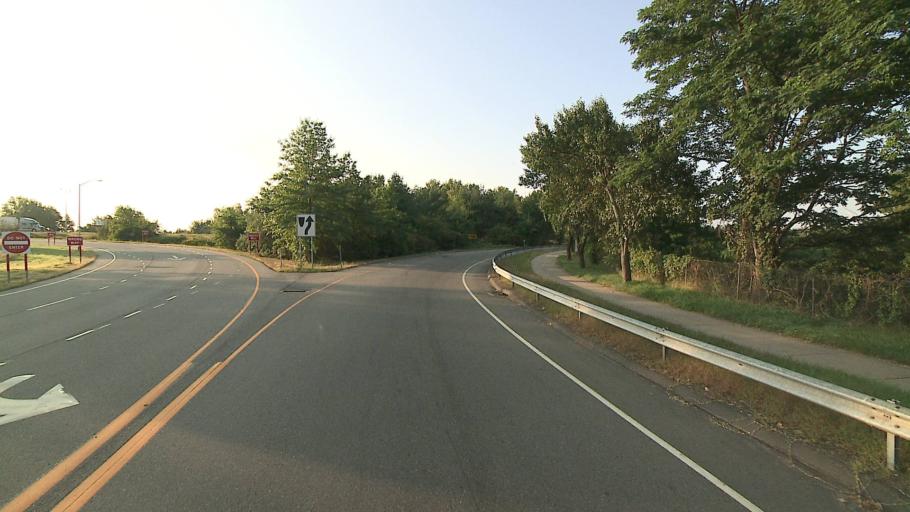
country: US
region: Connecticut
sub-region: Hartford County
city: Hartford
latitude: 41.7588
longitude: -72.6472
